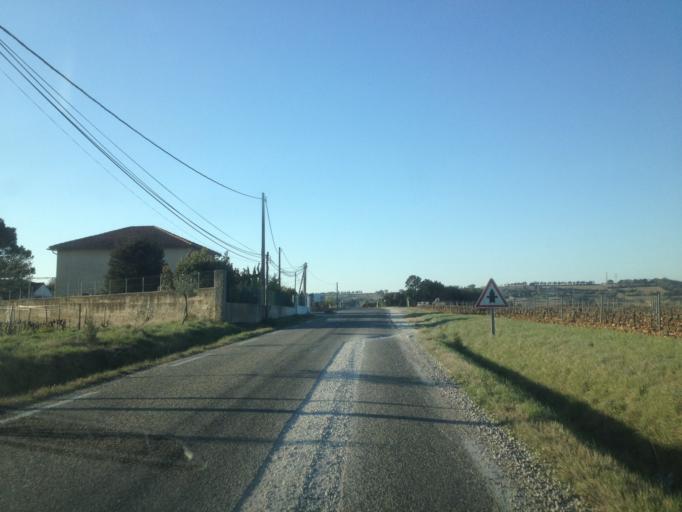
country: FR
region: Provence-Alpes-Cote d'Azur
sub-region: Departement du Vaucluse
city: Orange
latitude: 44.1051
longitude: 4.8202
